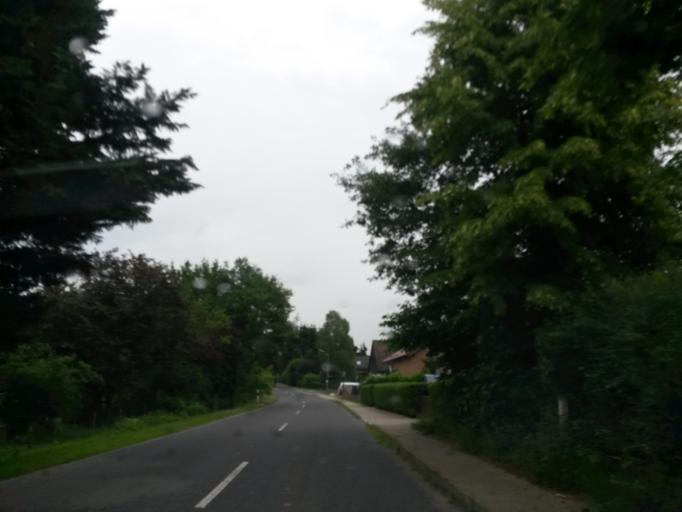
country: DE
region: North Rhine-Westphalia
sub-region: Regierungsbezirk Koln
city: Overath
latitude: 50.8929
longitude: 7.3362
